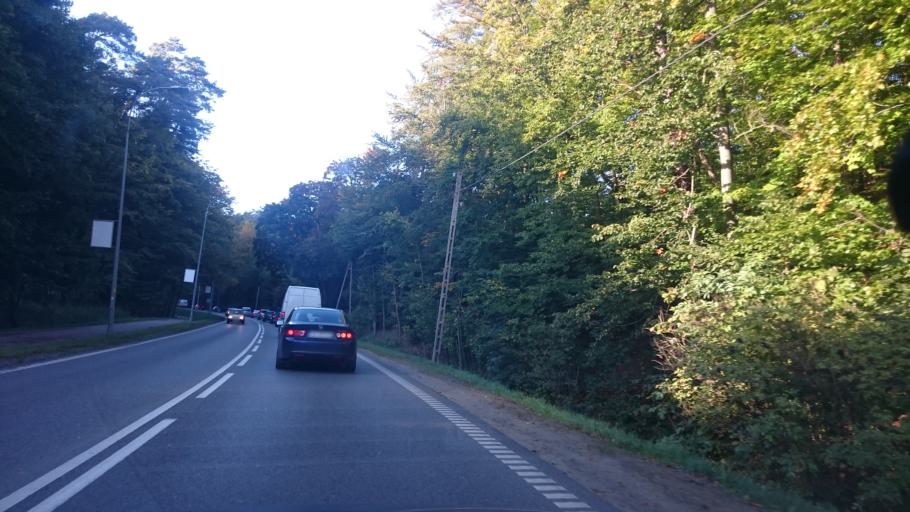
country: PL
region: Pomeranian Voivodeship
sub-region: Sopot
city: Sopot
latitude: 54.4145
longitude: 18.5467
